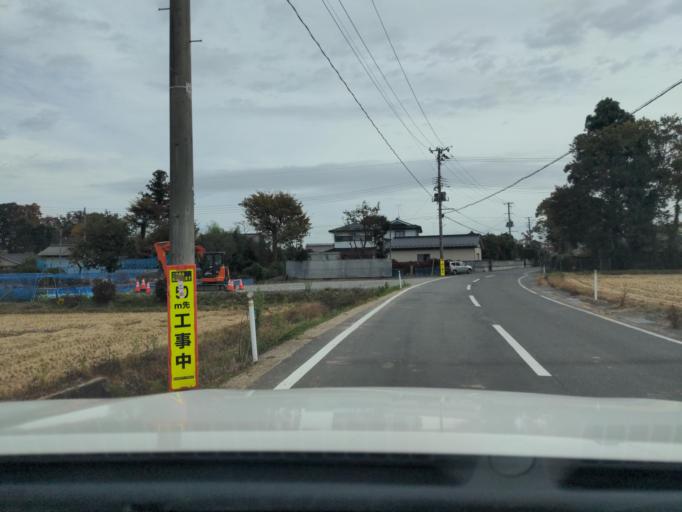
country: JP
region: Fukushima
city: Koriyama
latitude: 37.3471
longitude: 140.2839
